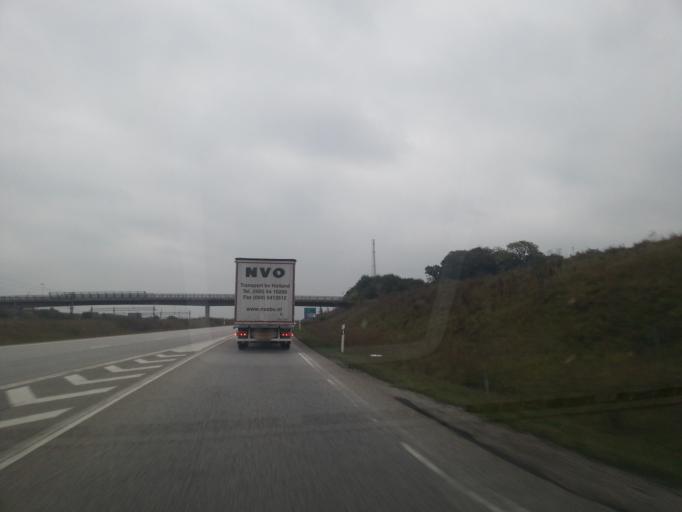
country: SE
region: Skane
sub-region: Malmo
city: Tygelsjo
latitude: 55.5472
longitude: 13.0099
